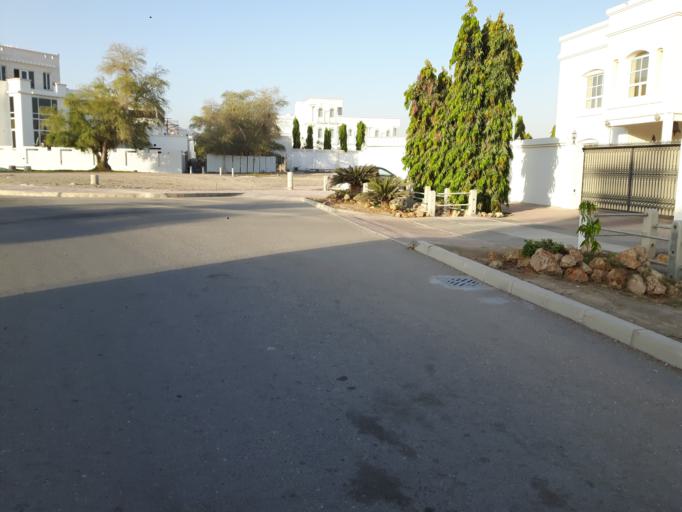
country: OM
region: Muhafazat Masqat
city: Bawshar
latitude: 23.6105
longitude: 58.4517
